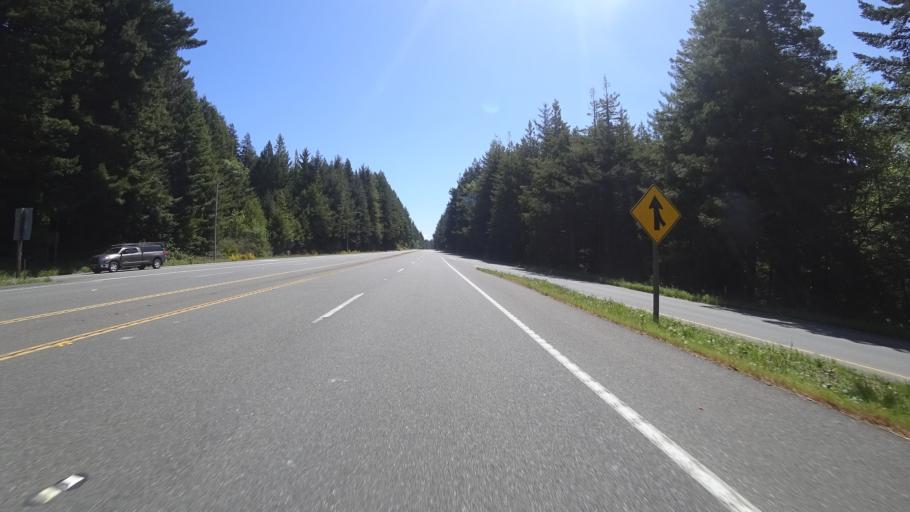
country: US
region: California
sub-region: Humboldt County
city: Westhaven-Moonstone
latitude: 41.0617
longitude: -124.1387
